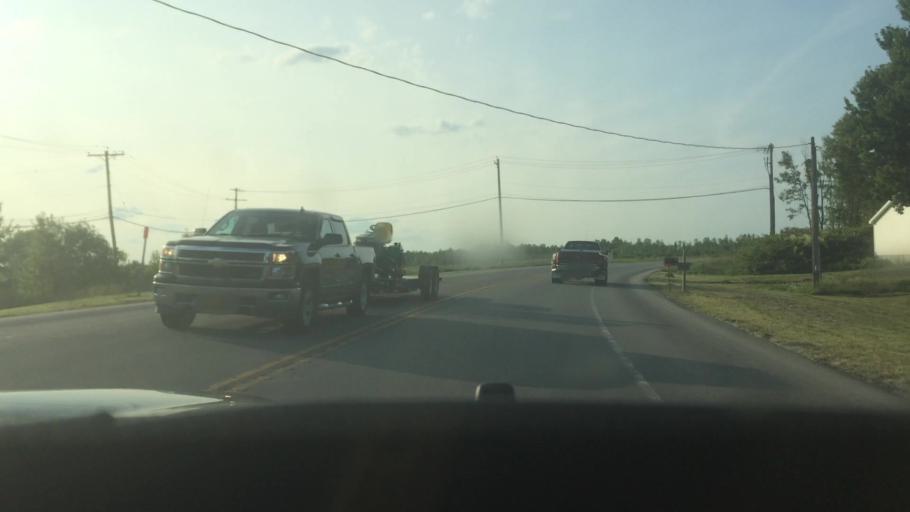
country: US
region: New York
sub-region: St. Lawrence County
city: Ogdensburg
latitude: 44.6823
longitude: -75.4453
